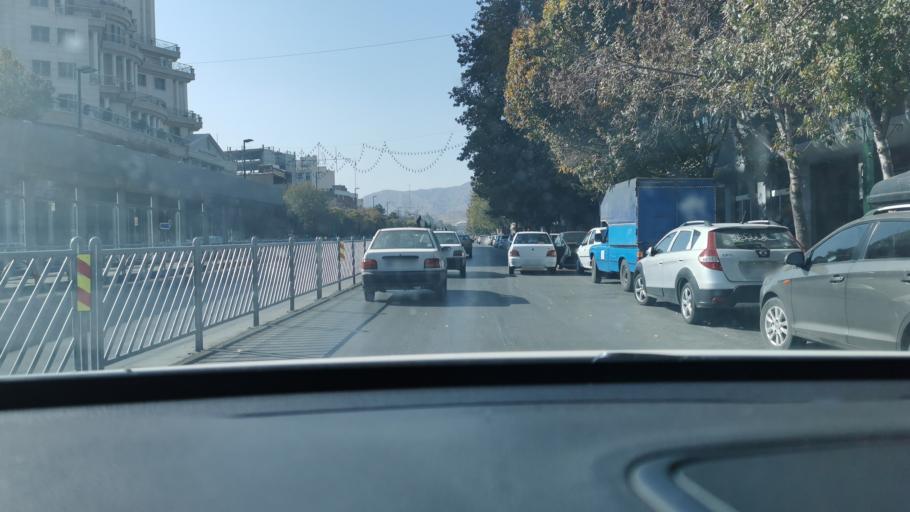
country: IR
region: Razavi Khorasan
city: Mashhad
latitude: 36.2731
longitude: 59.6029
